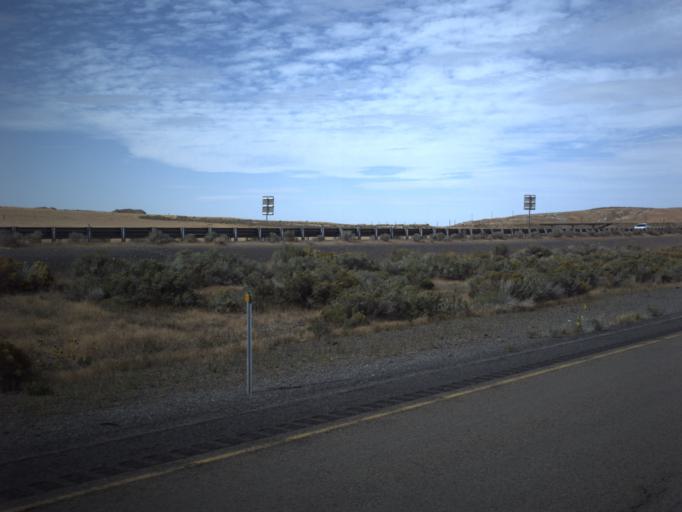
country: US
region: Utah
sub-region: Tooele County
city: Grantsville
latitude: 40.8223
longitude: -112.8908
